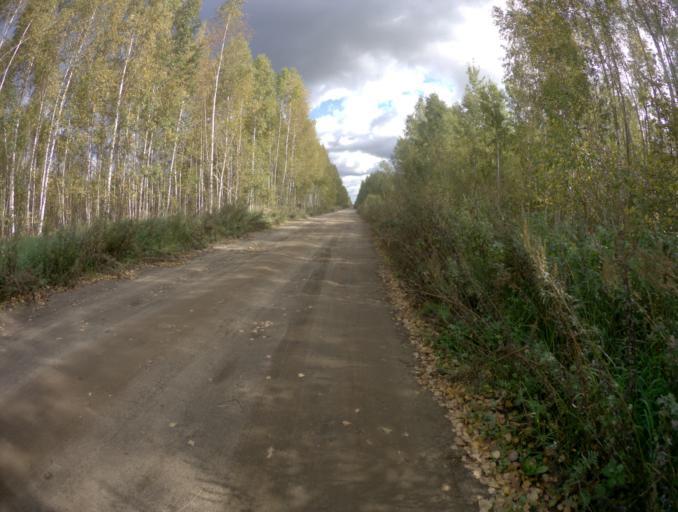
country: RU
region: Moskovskaya
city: Baksheyevo
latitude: 55.7148
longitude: 39.9107
